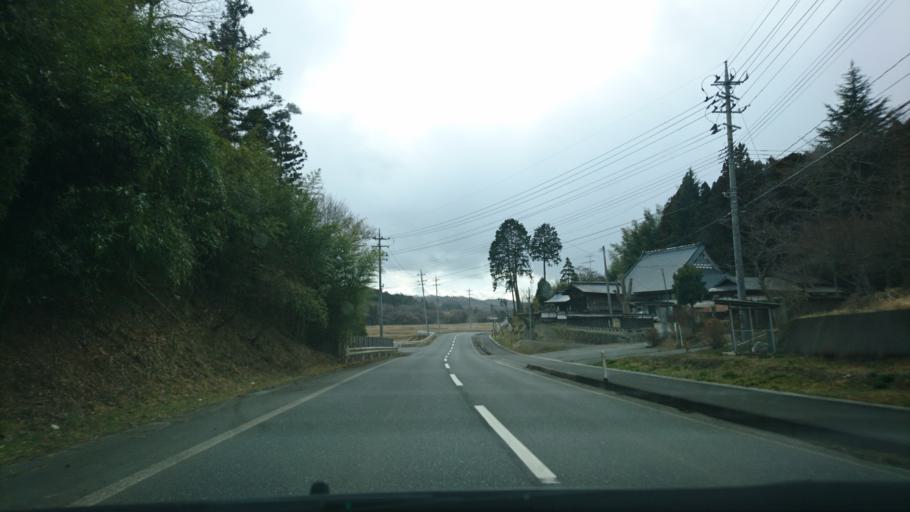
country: JP
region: Iwate
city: Ichinoseki
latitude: 38.8246
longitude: 141.1717
